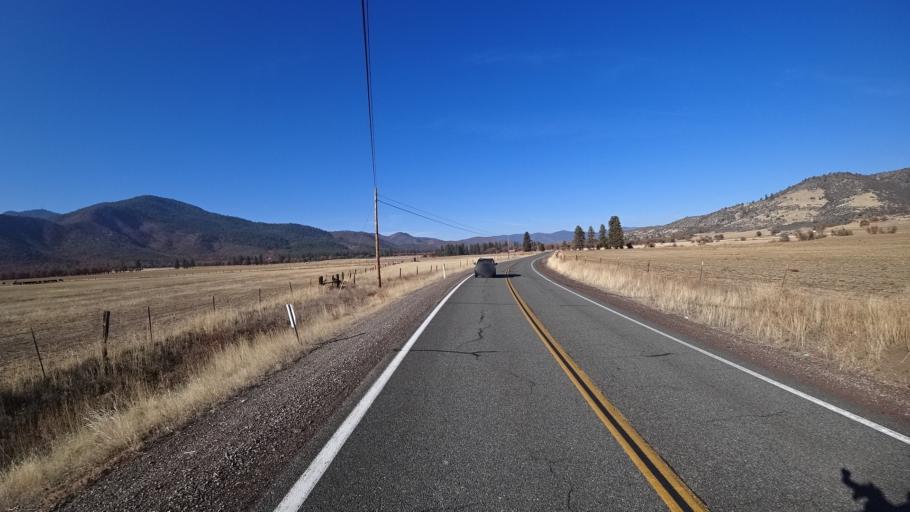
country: US
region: California
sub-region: Siskiyou County
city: Montague
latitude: 41.6550
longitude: -122.5771
